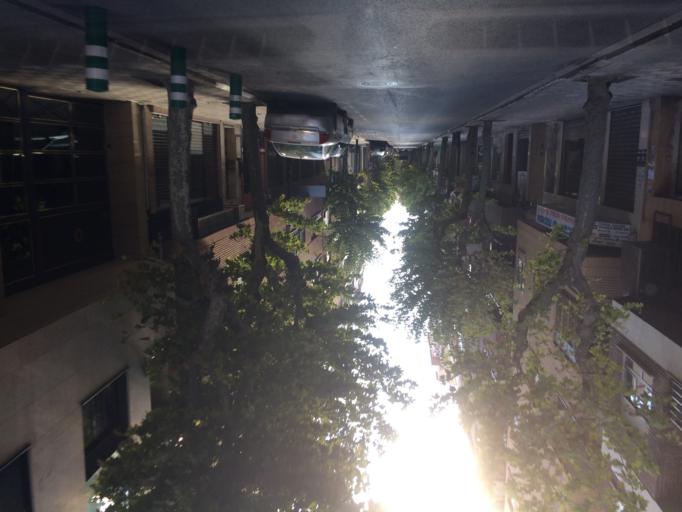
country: ES
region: Castille-La Mancha
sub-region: Provincia de Albacete
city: Albacete
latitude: 38.9942
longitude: -1.8614
